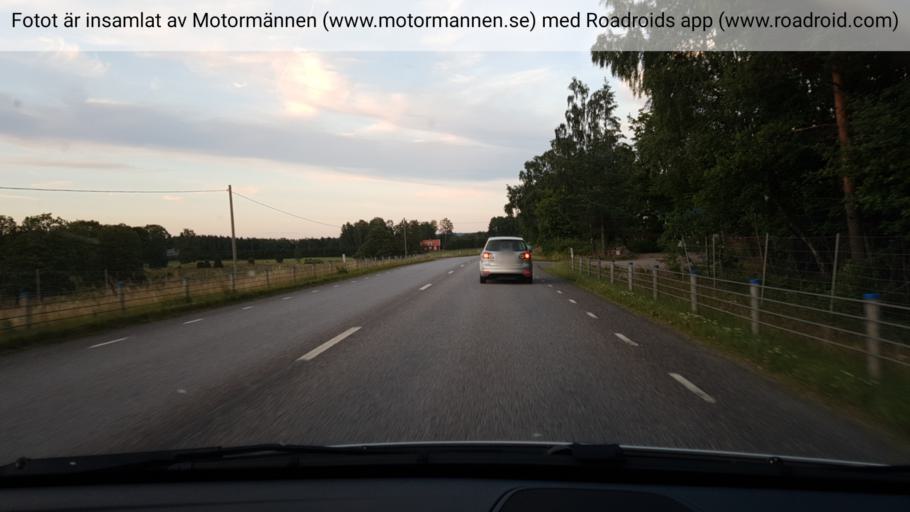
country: SE
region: Vaestra Goetaland
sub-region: Tibro Kommun
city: Tibro
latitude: 58.4164
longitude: 14.1027
